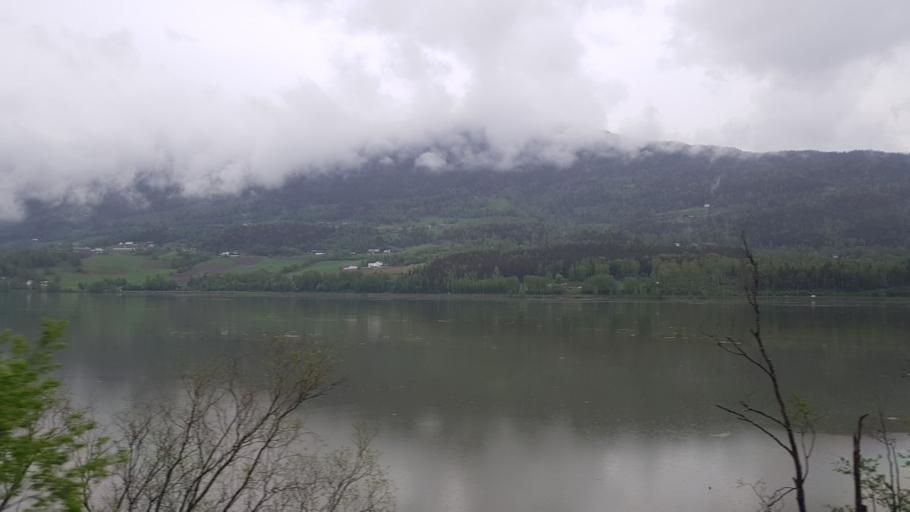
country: NO
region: Oppland
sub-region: Ringebu
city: Ringebu
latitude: 61.4279
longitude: 10.2250
